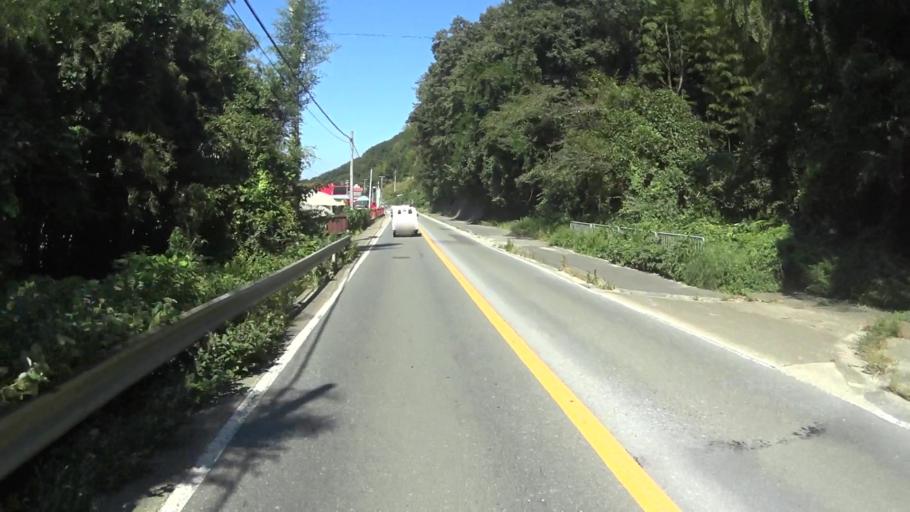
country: JP
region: Kyoto
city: Ayabe
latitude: 35.2884
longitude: 135.2853
